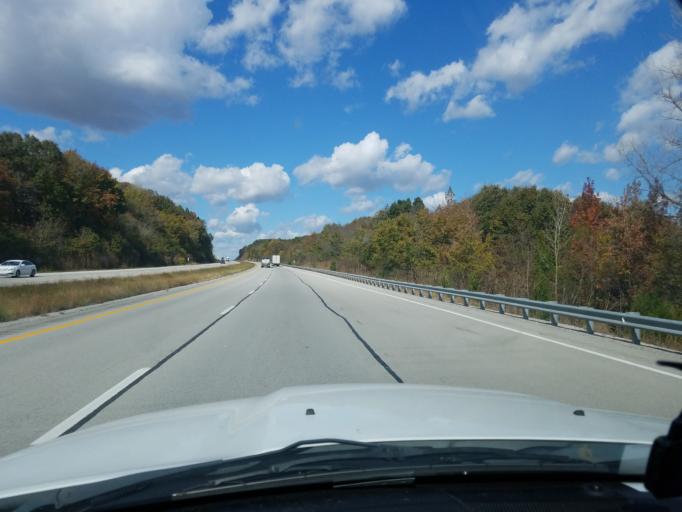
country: US
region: Kentucky
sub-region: Butler County
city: Morgantown
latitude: 37.2196
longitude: -86.7143
